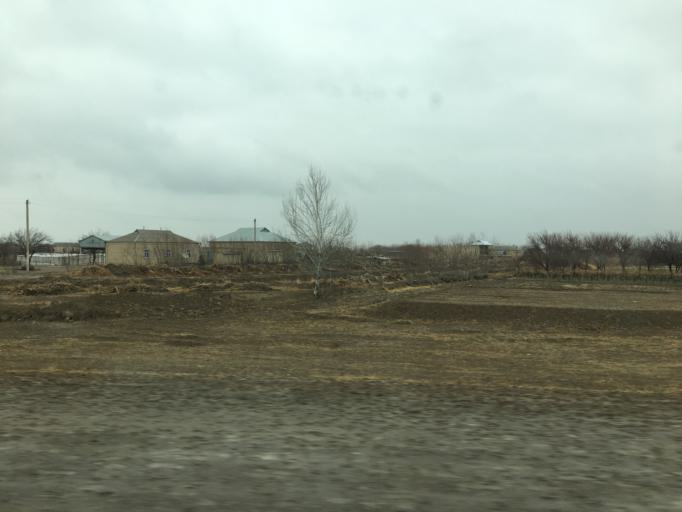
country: TM
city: Murgab
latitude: 37.4710
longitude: 62.0274
